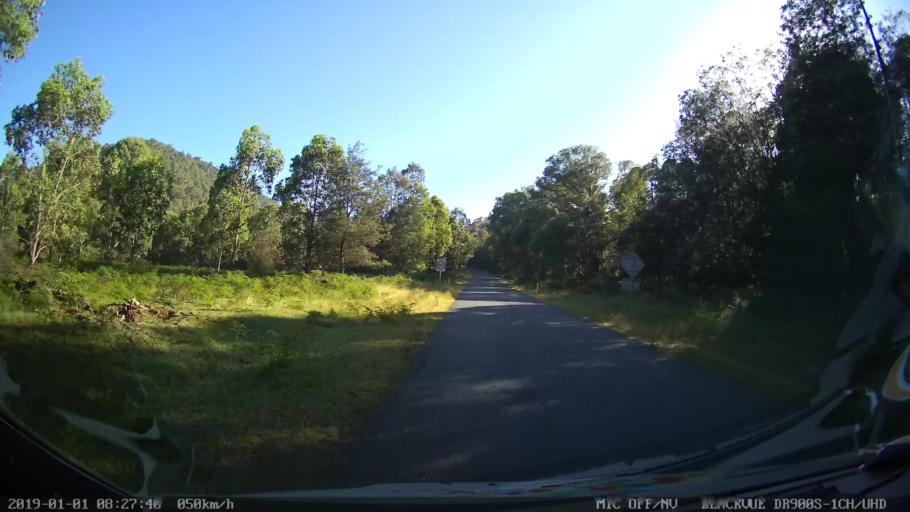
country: AU
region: New South Wales
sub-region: Snowy River
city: Jindabyne
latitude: -36.3800
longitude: 148.1850
